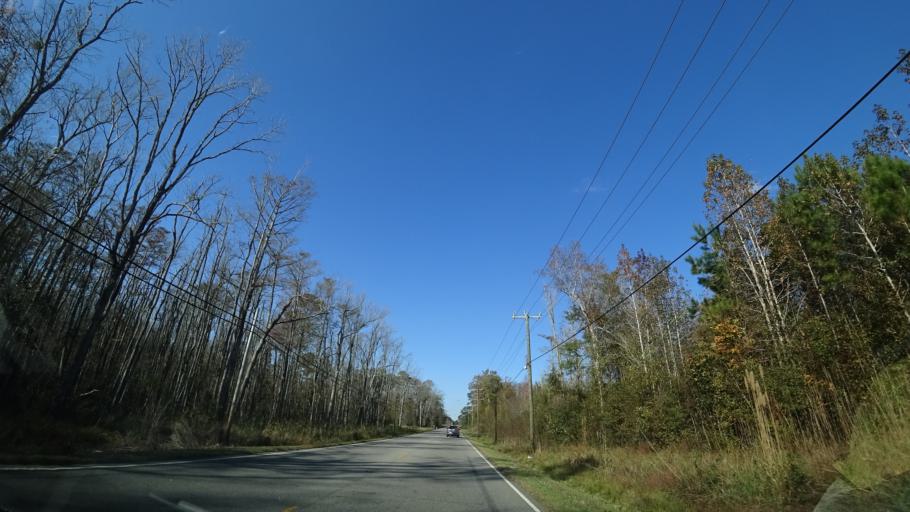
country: US
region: North Carolina
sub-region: Currituck County
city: Moyock
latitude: 36.5838
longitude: -76.2038
